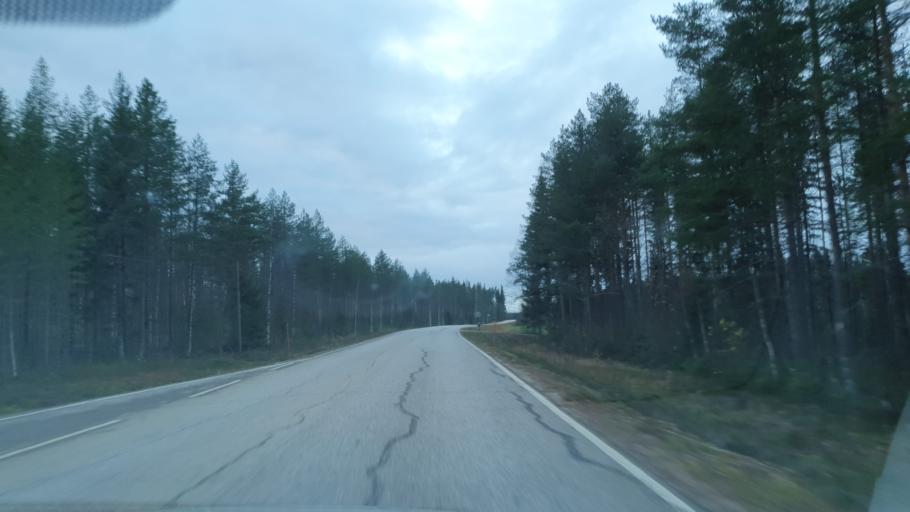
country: FI
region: Kainuu
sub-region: Kajaani
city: Ristijaervi
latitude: 64.4221
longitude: 28.4041
